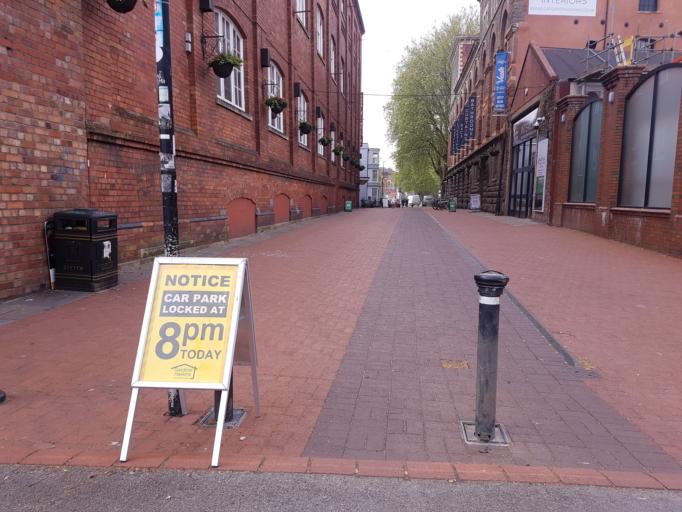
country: GB
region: England
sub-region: Bristol
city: Bristol
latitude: 51.4542
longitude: -2.5809
